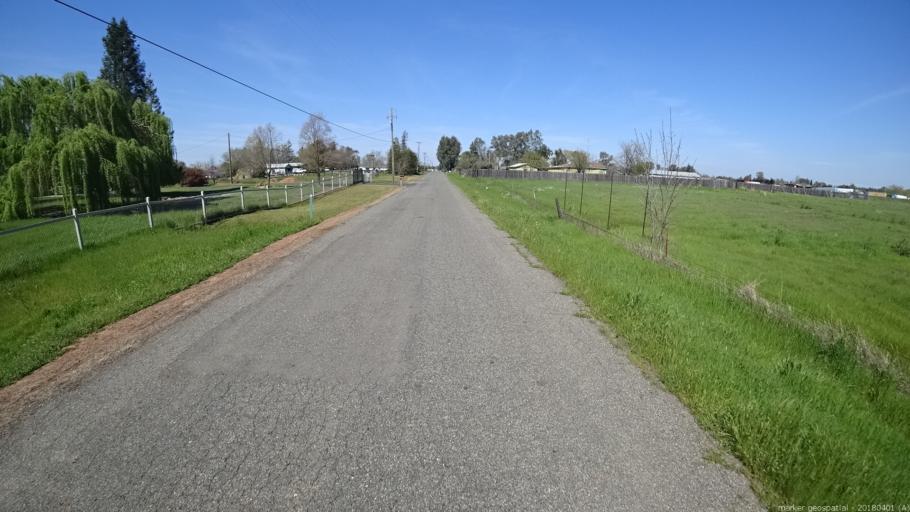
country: US
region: California
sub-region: Sacramento County
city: Wilton
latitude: 38.4035
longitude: -121.2286
